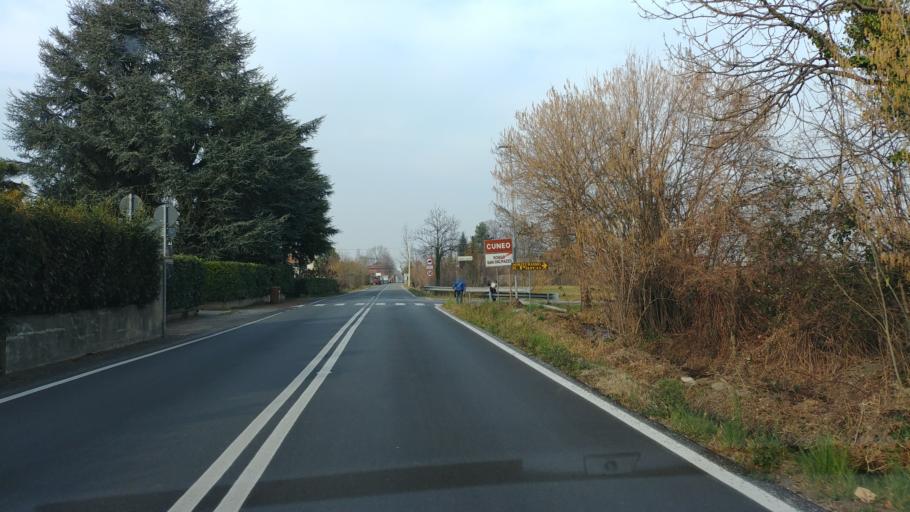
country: IT
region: Piedmont
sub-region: Provincia di Cuneo
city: Borgo San Dalmazzo
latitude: 44.3527
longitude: 7.5146
